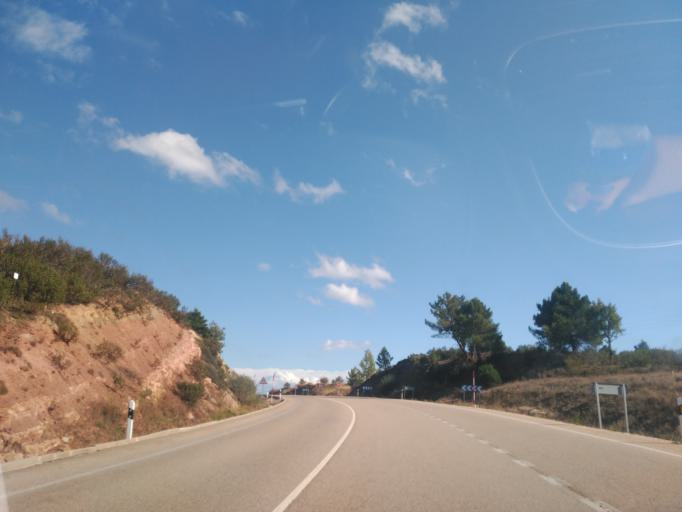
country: ES
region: Castille and Leon
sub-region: Provincia de Burgos
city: Pinilla de los Barruecos
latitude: 41.8997
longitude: -3.2707
